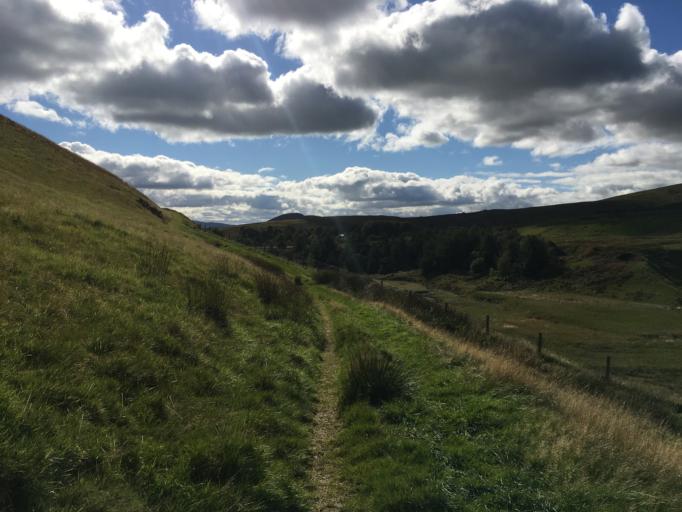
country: GB
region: Scotland
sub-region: The Scottish Borders
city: West Linton
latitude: 55.7768
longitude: -3.3866
